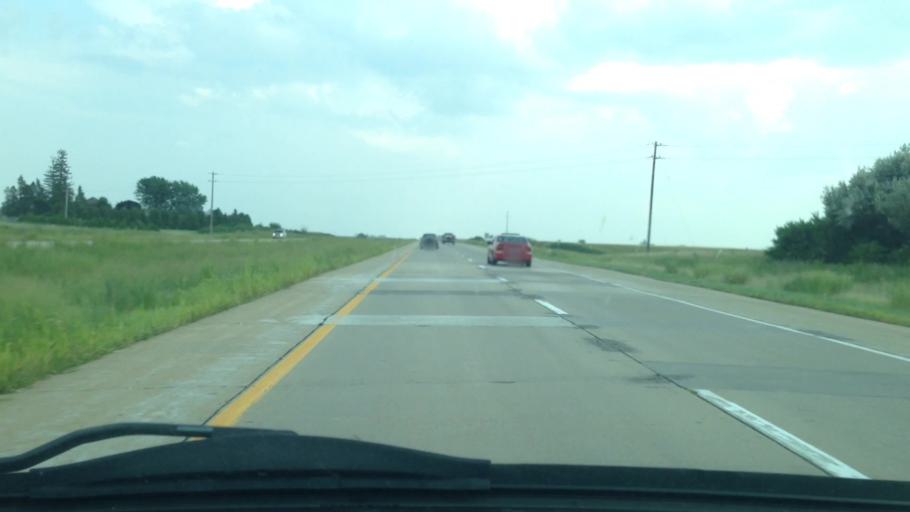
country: US
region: Iowa
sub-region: Black Hawk County
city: La Porte City
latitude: 42.3998
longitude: -92.1510
